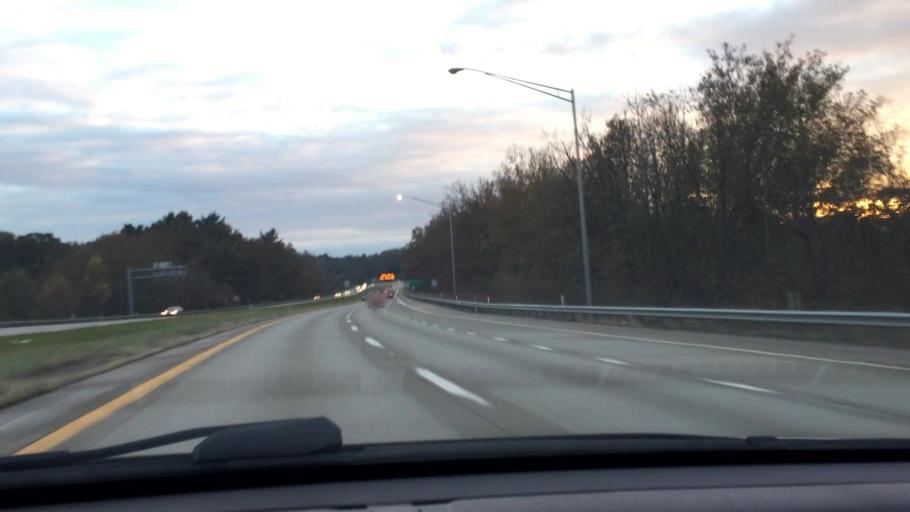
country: US
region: Pennsylvania
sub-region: Washington County
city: McGovern
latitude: 40.2188
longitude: -80.2154
